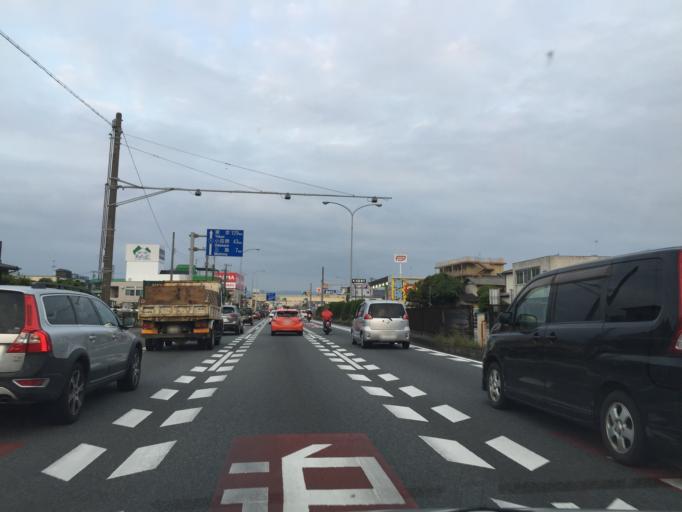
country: JP
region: Shizuoka
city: Numazu
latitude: 35.1216
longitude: 138.8611
